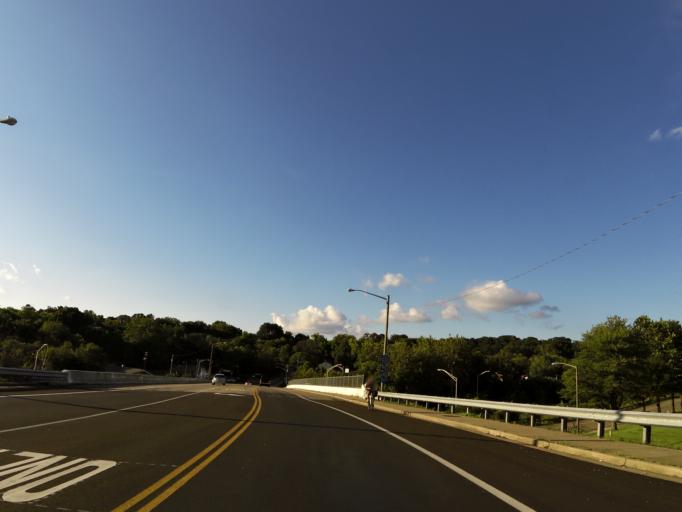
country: US
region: Tennessee
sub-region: Knox County
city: Knoxville
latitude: 36.0029
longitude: -83.9541
